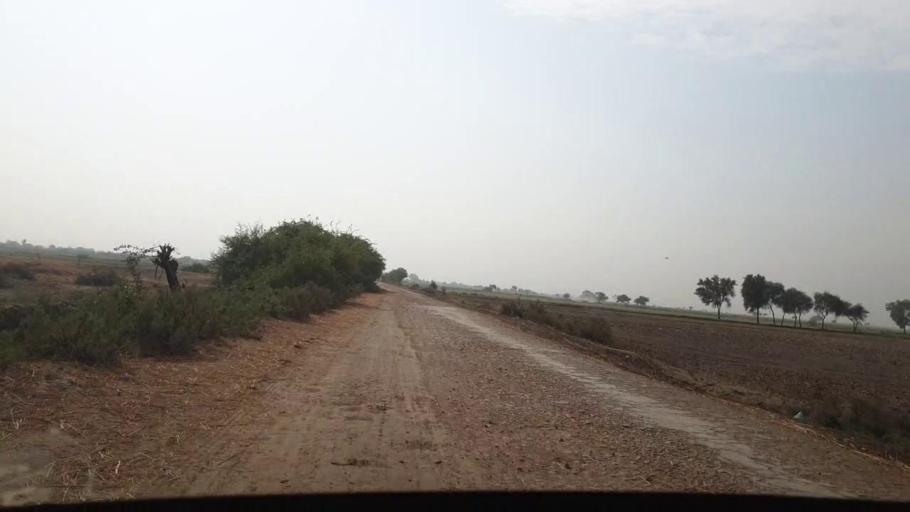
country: PK
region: Sindh
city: Chuhar Jamali
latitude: 24.3846
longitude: 67.9387
